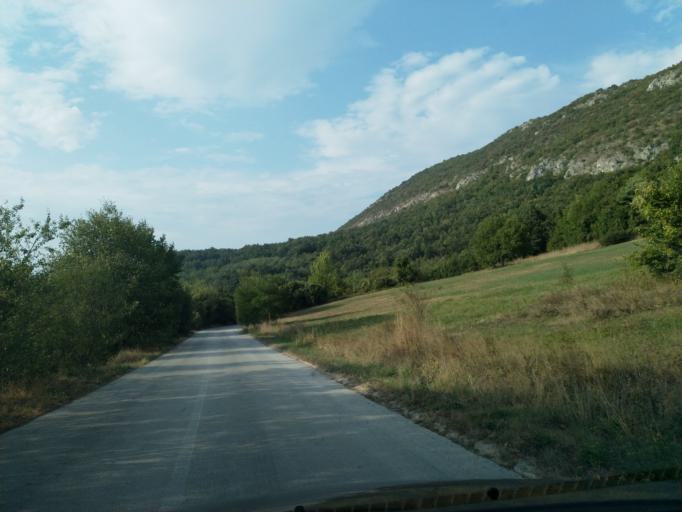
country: RS
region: Central Serbia
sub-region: Pomoravski Okrug
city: Paracin
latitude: 43.8380
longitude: 21.5389
